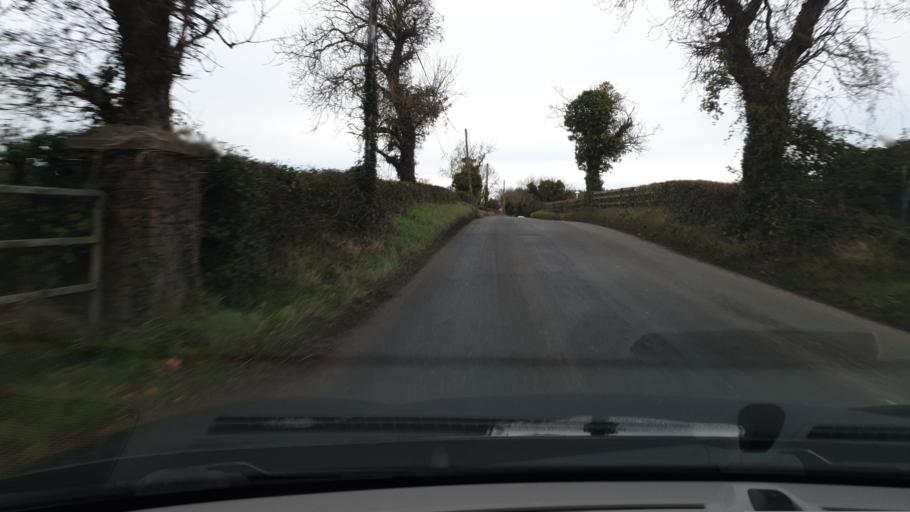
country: IE
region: Leinster
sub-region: An Mhi
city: Ashbourne
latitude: 53.5263
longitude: -6.4098
